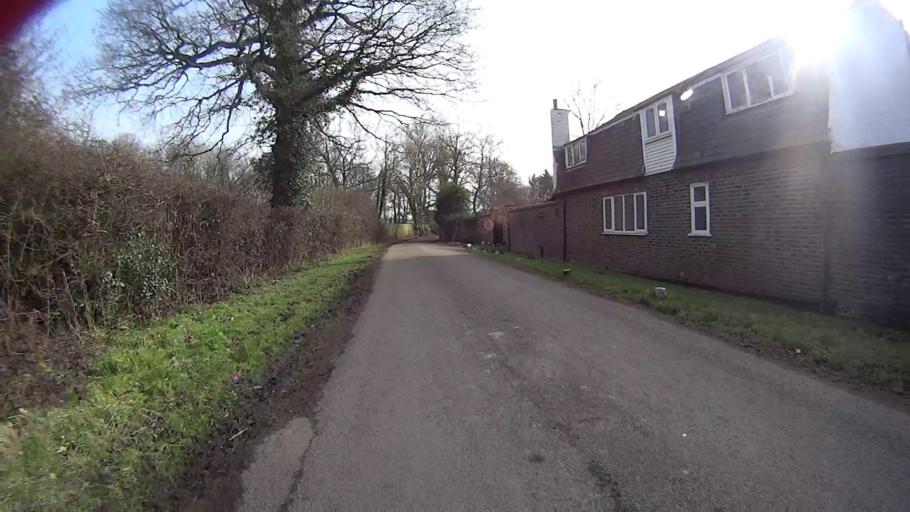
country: GB
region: England
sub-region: West Sussex
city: Copthorne
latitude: 51.1730
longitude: -0.1028
